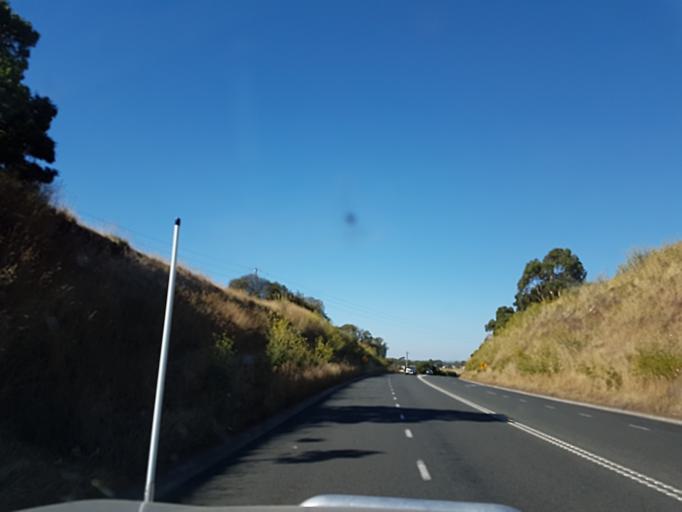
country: AU
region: Victoria
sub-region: Colac-Otway
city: Colac
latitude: -38.3296
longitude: 143.6208
